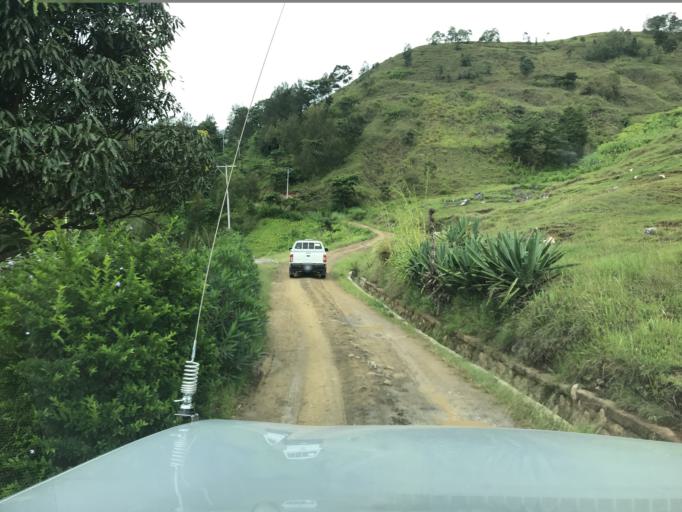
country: TL
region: Aileu
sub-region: Aileu Villa
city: Aileu
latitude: -8.8569
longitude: 125.5768
